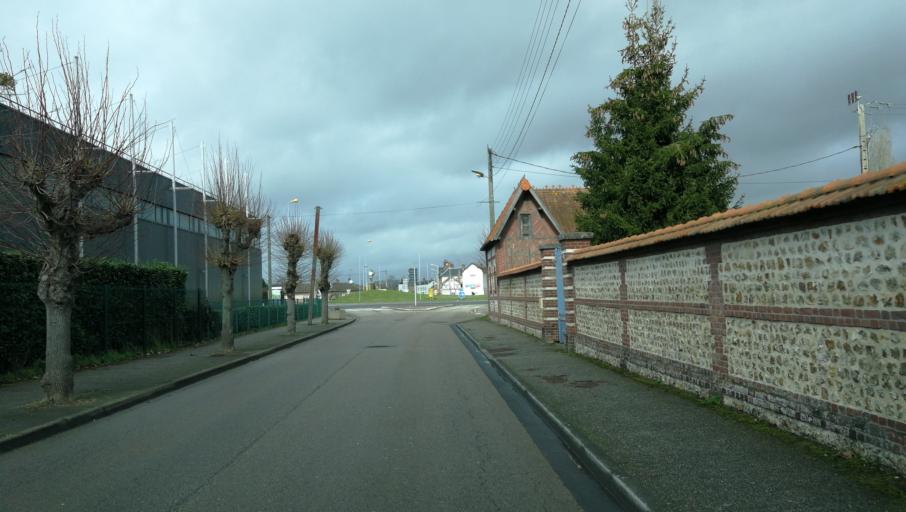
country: FR
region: Haute-Normandie
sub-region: Departement de l'Eure
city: Brionne
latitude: 49.1989
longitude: 0.7162
